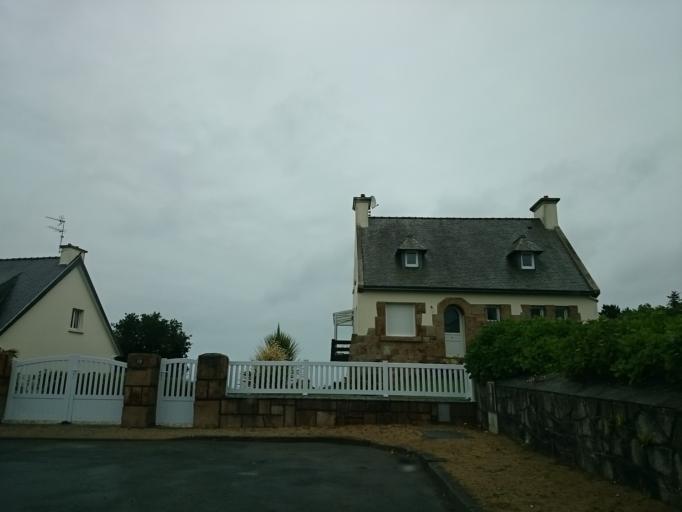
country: FR
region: Brittany
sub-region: Departement des Cotes-d'Armor
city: Louannec
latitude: 48.7970
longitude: -3.4100
